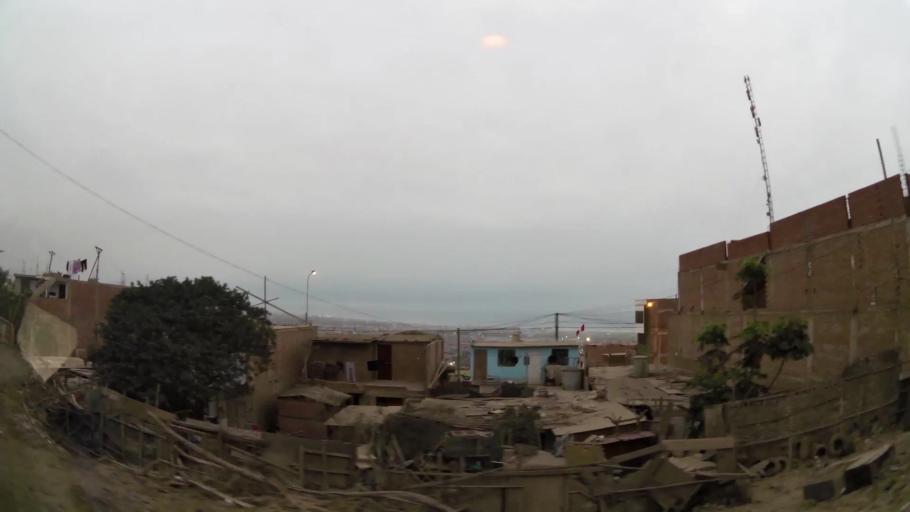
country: PE
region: Lima
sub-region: Lima
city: Surco
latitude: -12.1937
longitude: -77.0258
